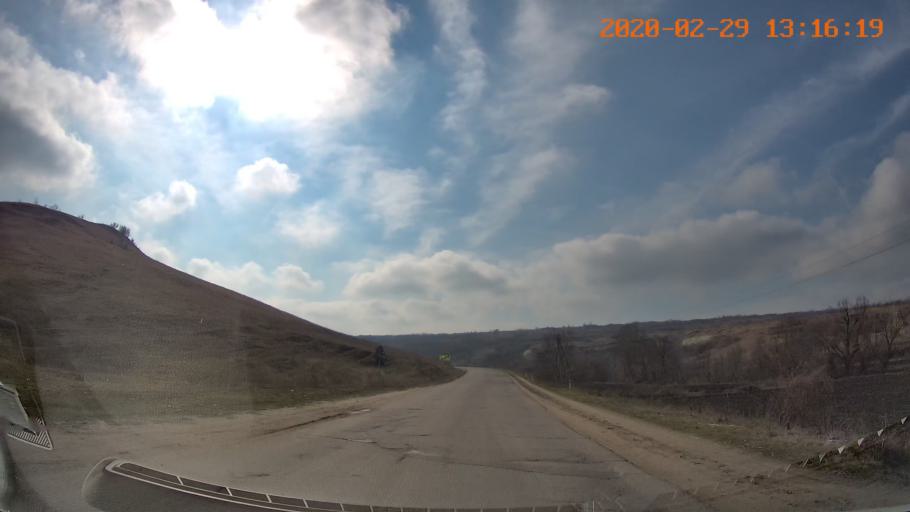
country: MD
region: Telenesti
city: Camenca
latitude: 48.0033
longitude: 28.6651
